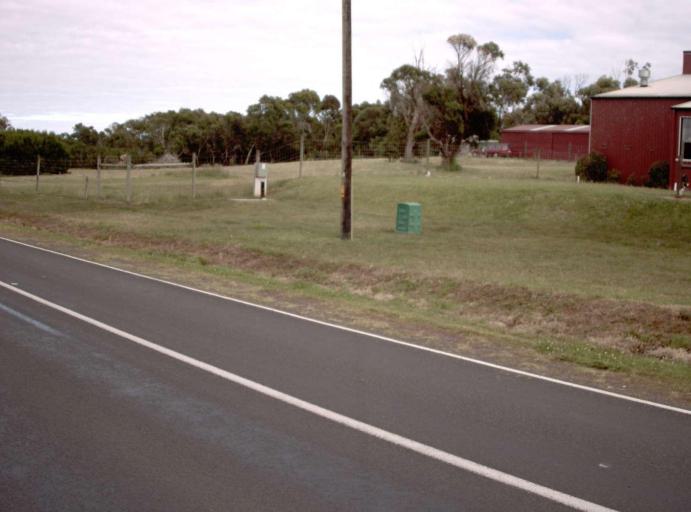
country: AU
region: Victoria
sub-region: Bass Coast
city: Phillip Island
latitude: -38.5154
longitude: 145.3453
